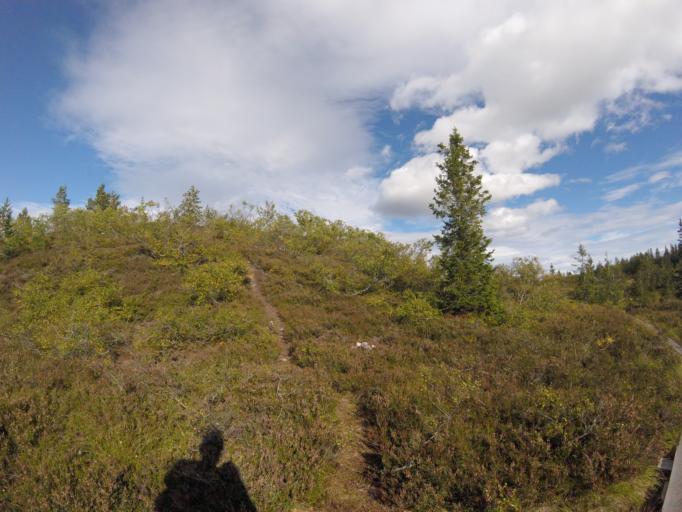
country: NO
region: Buskerud
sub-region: Flesberg
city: Lampeland
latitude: 59.7614
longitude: 9.4256
